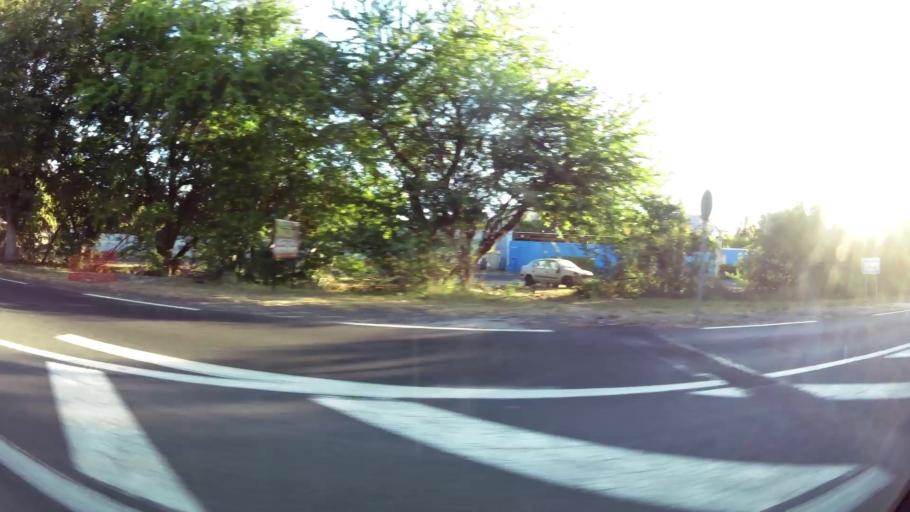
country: RE
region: Reunion
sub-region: Reunion
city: Trois-Bassins
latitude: -21.0902
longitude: 55.2347
